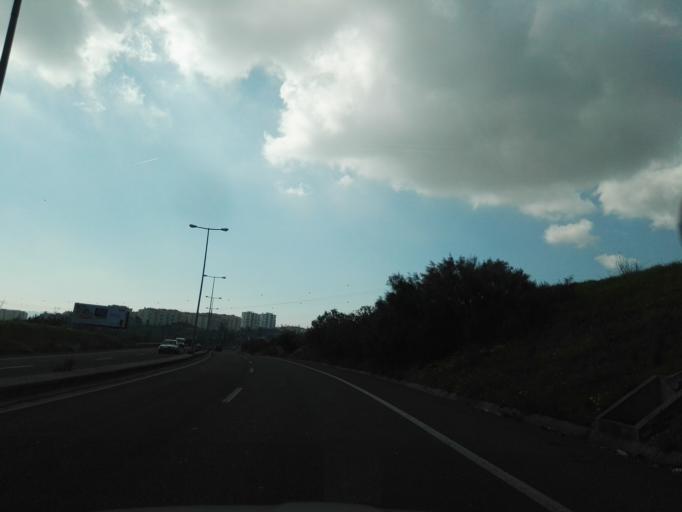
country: PT
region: Lisbon
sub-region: Odivelas
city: Povoa de Santo Adriao
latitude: 38.8063
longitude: -9.1708
